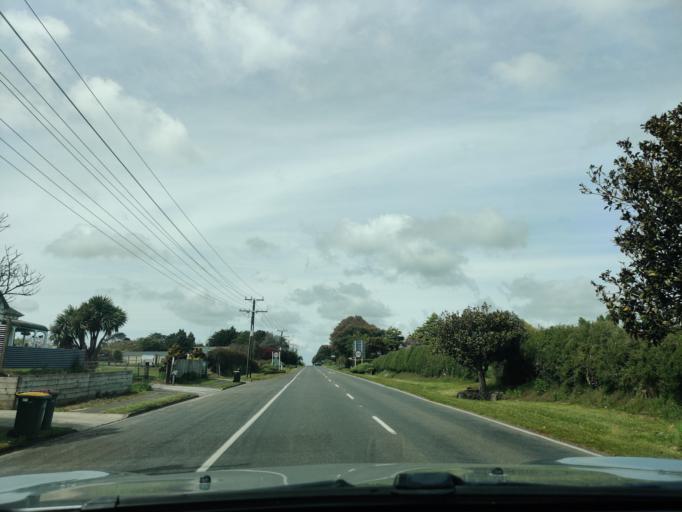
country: NZ
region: Taranaki
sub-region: South Taranaki District
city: Eltham
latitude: -39.4287
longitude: 174.1552
